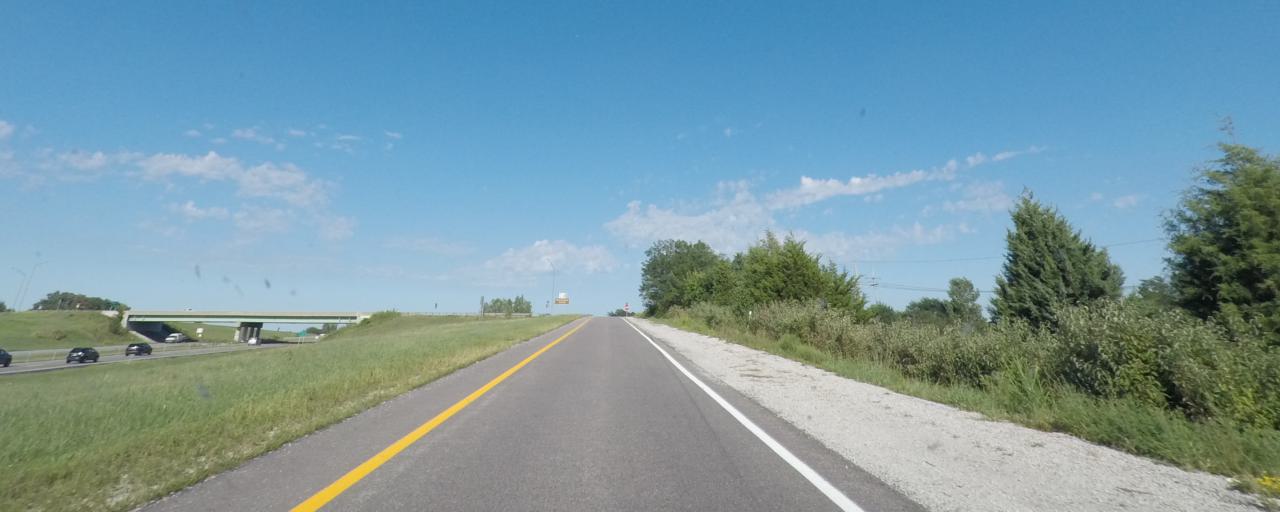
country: US
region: Missouri
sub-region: Clay County
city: Gladstone
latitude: 39.2552
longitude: -94.6029
